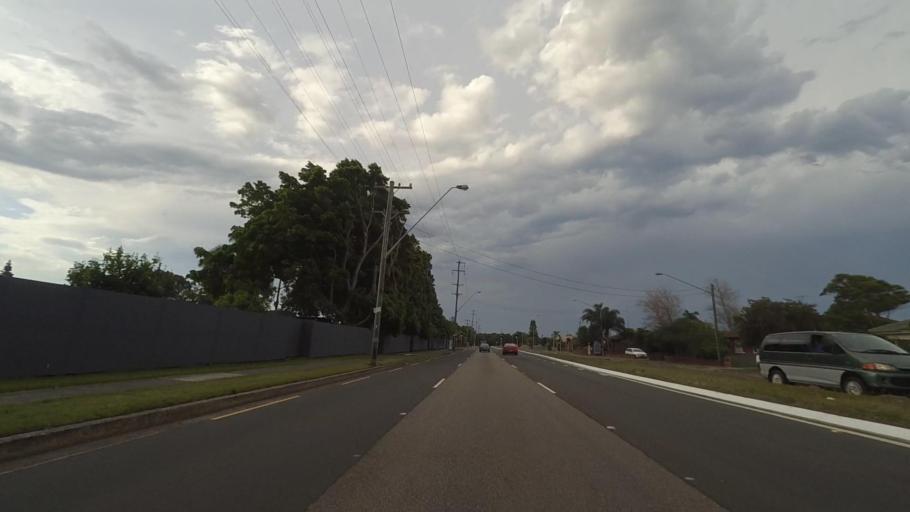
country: AU
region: New South Wales
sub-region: Shellharbour
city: Lake Illawarra
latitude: -34.5270
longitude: 150.8695
